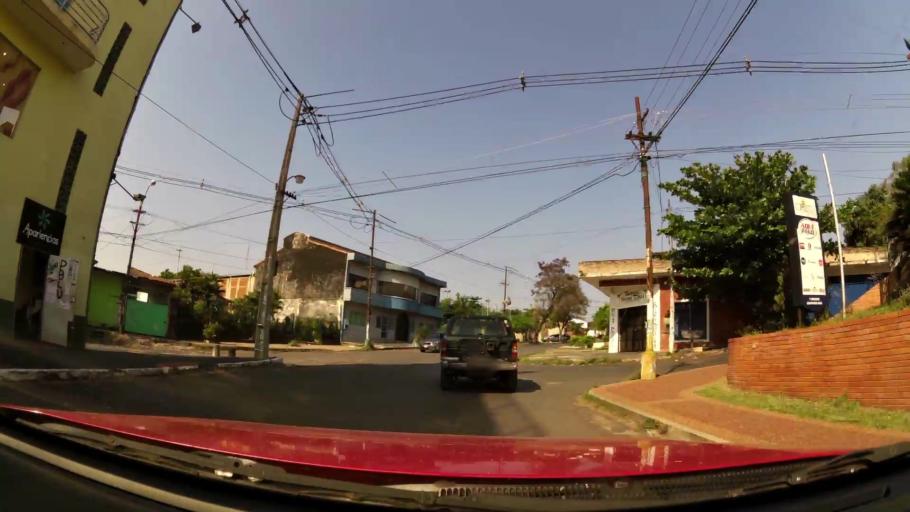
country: PY
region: Asuncion
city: Asuncion
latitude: -25.3175
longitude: -57.6332
